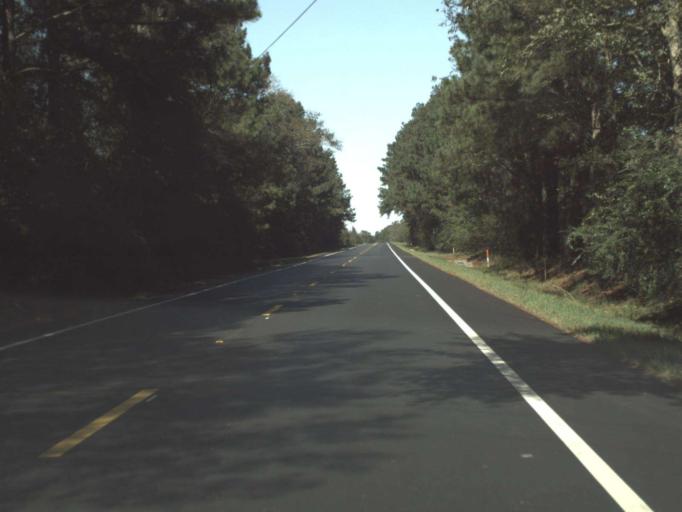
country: US
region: Alabama
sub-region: Covington County
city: Florala
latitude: 30.8623
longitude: -86.2515
